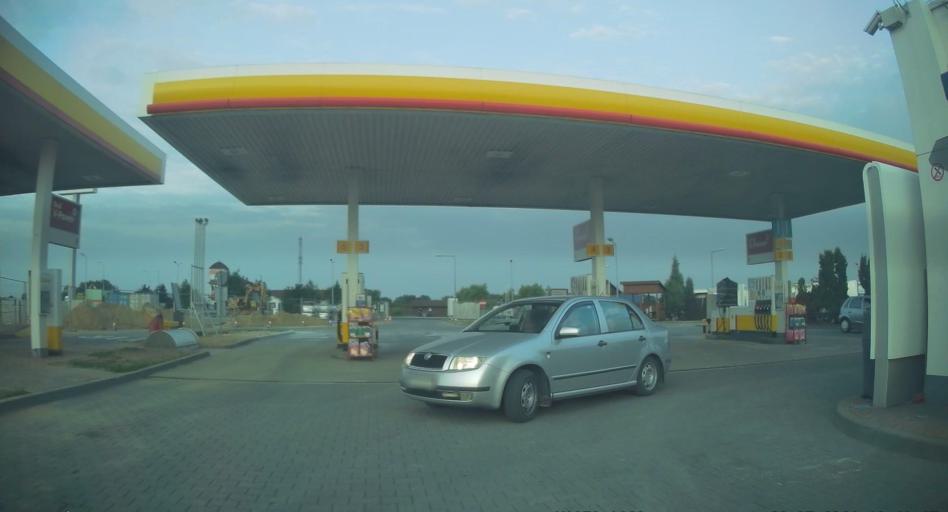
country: PL
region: Lodz Voivodeship
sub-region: Piotrkow Trybunalski
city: Piotrkow Trybunalski
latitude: 51.4413
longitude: 19.6796
